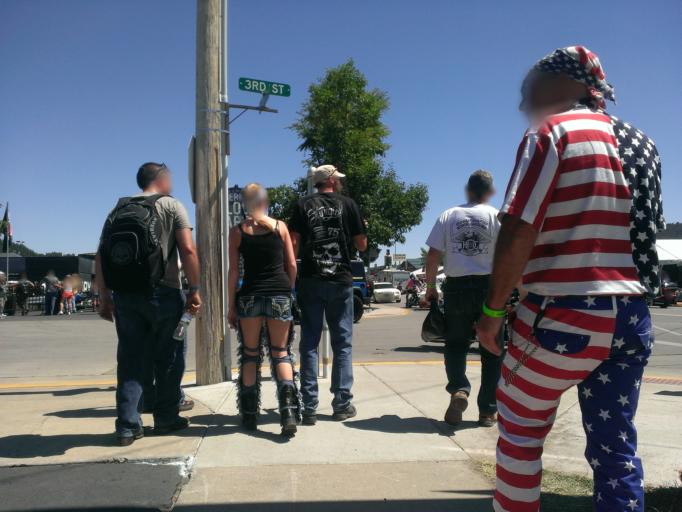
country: US
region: South Dakota
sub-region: Meade County
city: Sturgis
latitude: 44.4158
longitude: -103.5146
